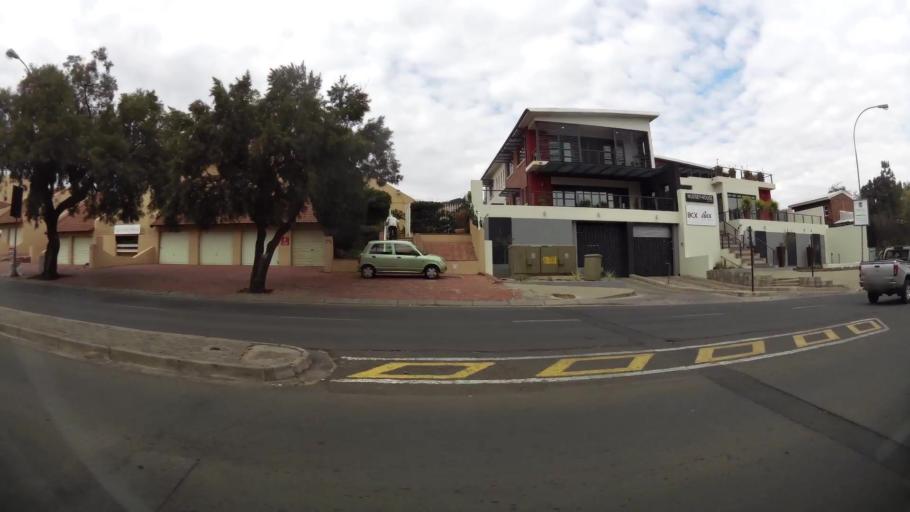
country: ZA
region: Orange Free State
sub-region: Mangaung Metropolitan Municipality
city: Bloemfontein
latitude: -29.1059
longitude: 26.2135
